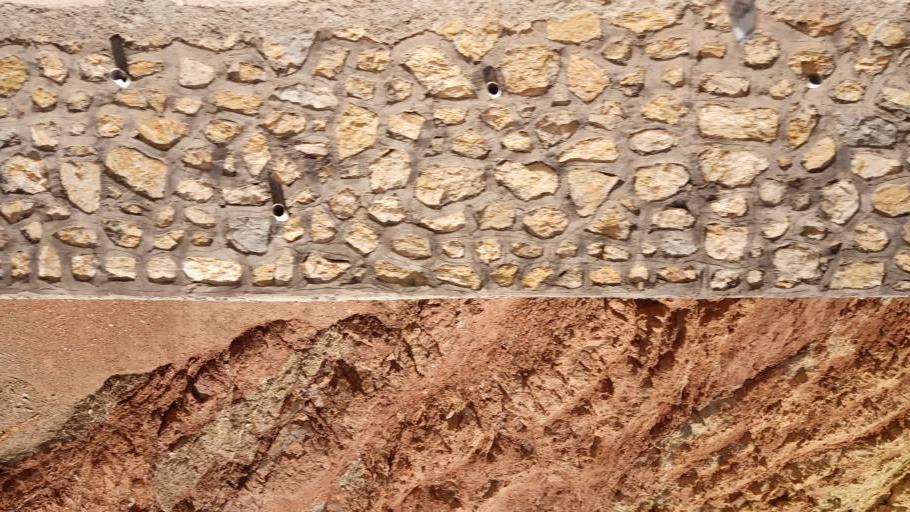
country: TR
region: Malatya
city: Darende
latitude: 38.6019
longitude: 37.4672
